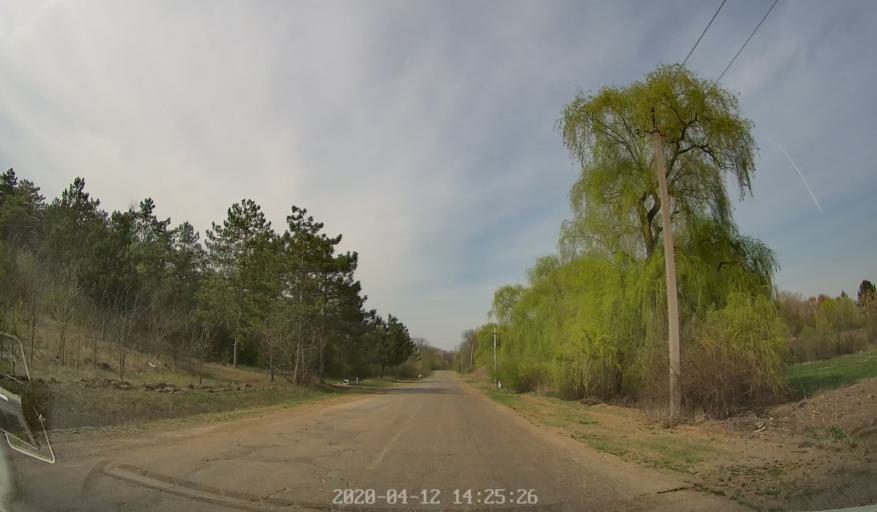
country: MD
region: Telenesti
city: Cocieri
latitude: 47.2708
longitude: 29.1237
